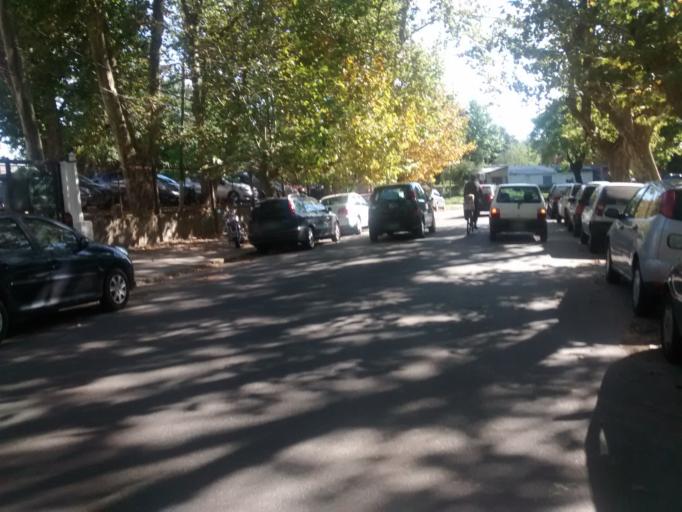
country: AR
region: Buenos Aires
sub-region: Partido de La Plata
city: La Plata
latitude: -34.9036
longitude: -57.9374
